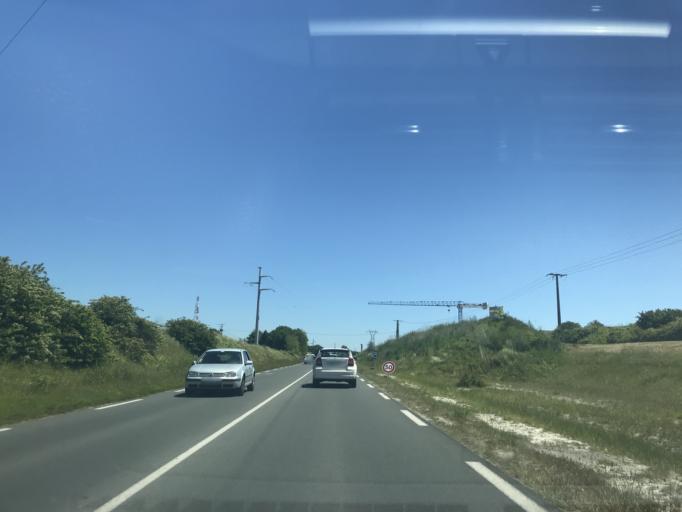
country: FR
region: Poitou-Charentes
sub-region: Departement de la Charente-Maritime
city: Royan
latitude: 45.6430
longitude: -1.0390
